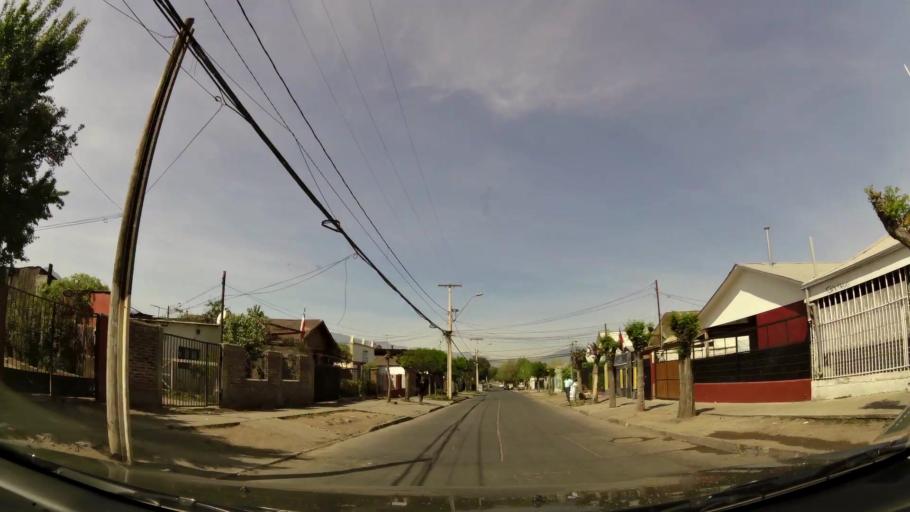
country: CL
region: Santiago Metropolitan
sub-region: Provincia de Cordillera
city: Puente Alto
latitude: -33.6213
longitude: -70.5807
